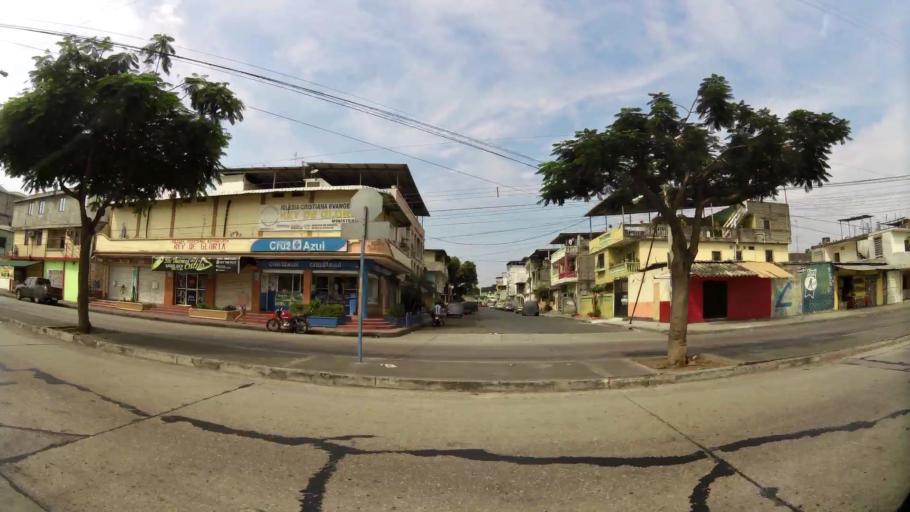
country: EC
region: Guayas
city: Guayaquil
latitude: -2.2457
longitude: -79.8999
